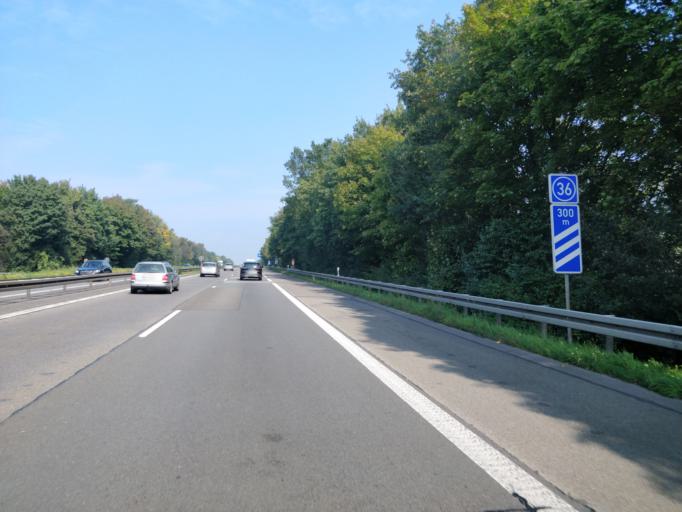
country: DE
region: North Rhine-Westphalia
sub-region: Regierungsbezirk Koln
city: Wahn-Heide
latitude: 50.8383
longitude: 7.0948
